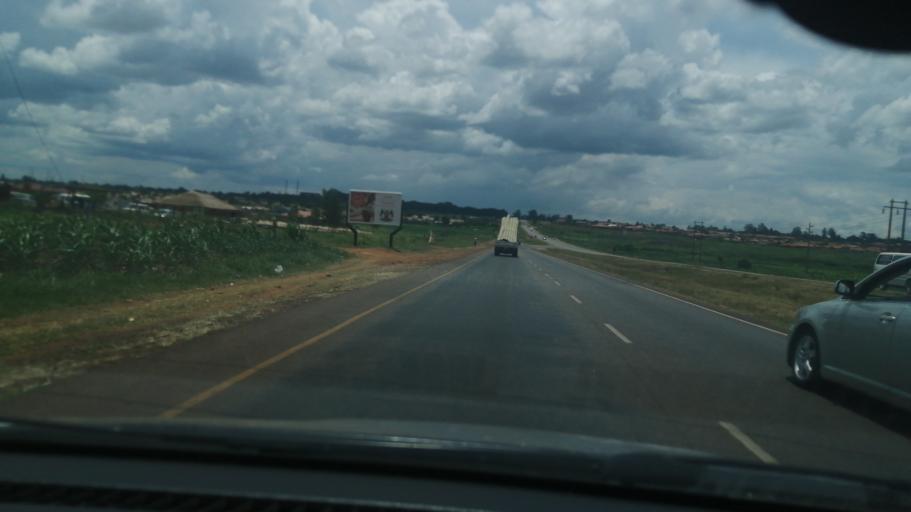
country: ZW
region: Harare
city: Harare
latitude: -17.8196
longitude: 30.9115
